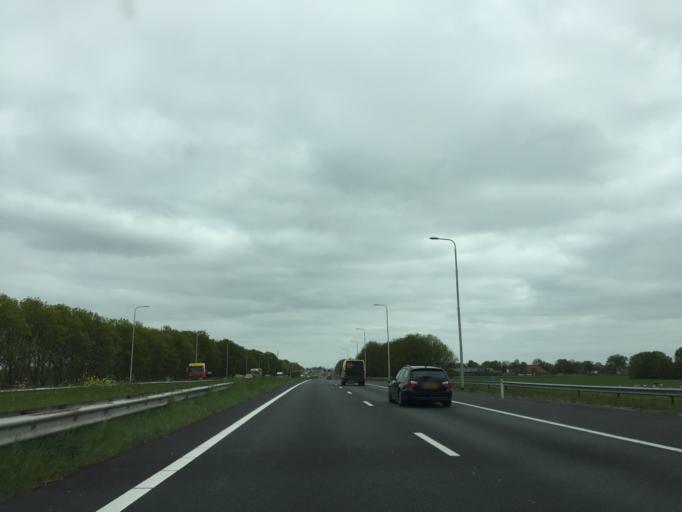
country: NL
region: North Holland
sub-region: Gemeente Beemster
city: Halfweg
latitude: 52.5709
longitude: 4.9717
